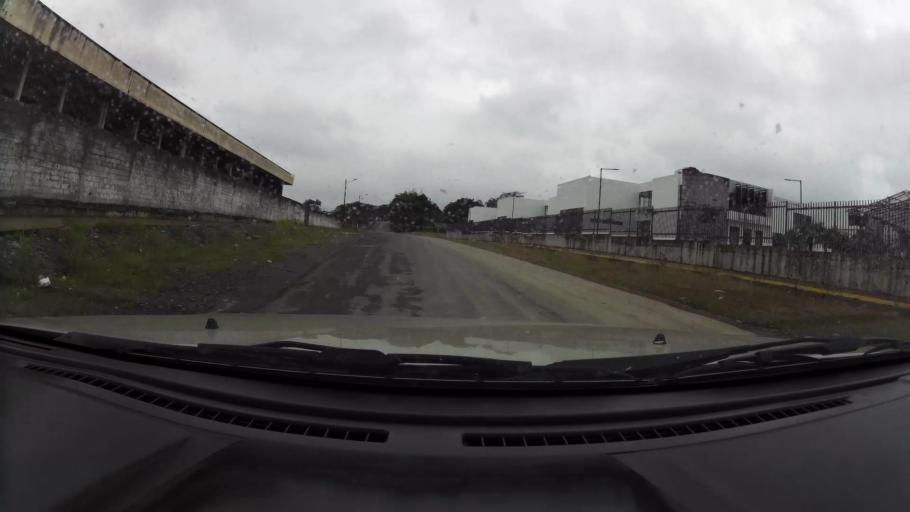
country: EC
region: Santo Domingo de los Tsachilas
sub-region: Canton Santo Domingo de los Colorados
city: Santo Domingo de los Colorados
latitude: -0.2503
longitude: -79.1476
